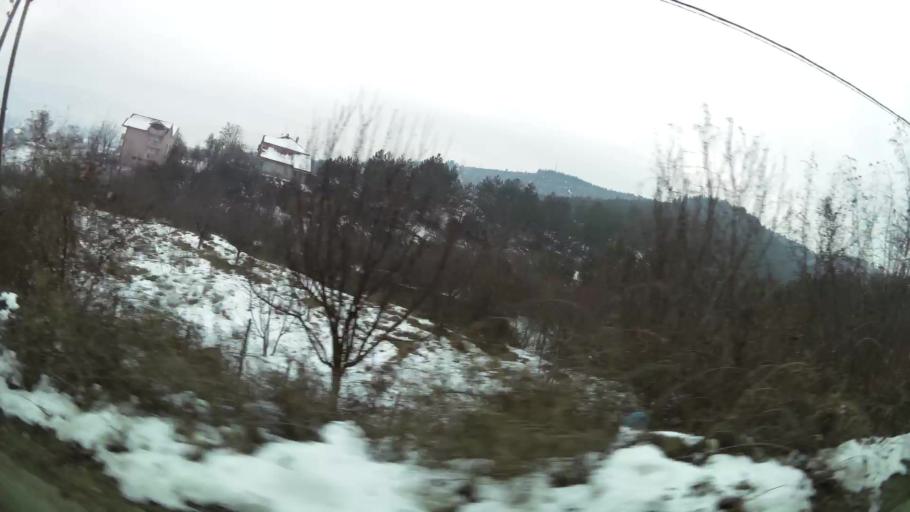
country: MK
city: Kondovo
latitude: 42.0146
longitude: 21.3072
